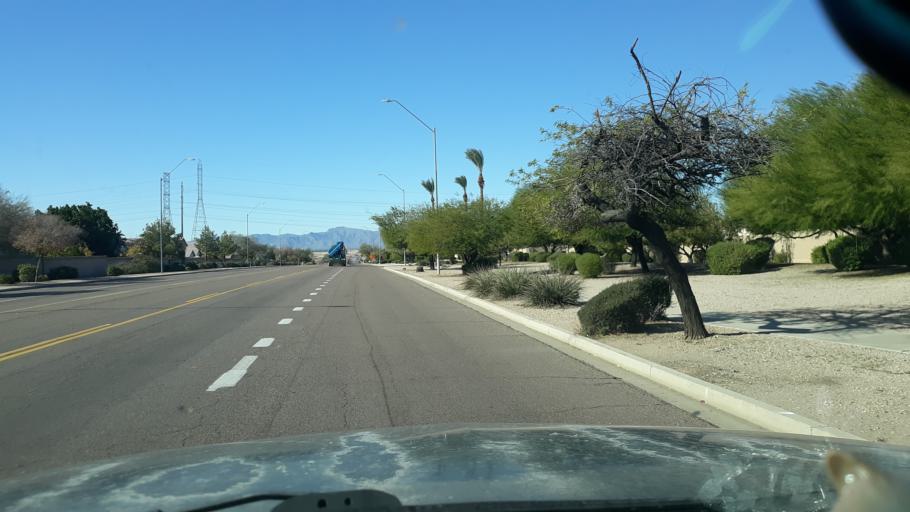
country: US
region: Arizona
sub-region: Maricopa County
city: Youngtown
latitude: 33.5511
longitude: -112.2947
